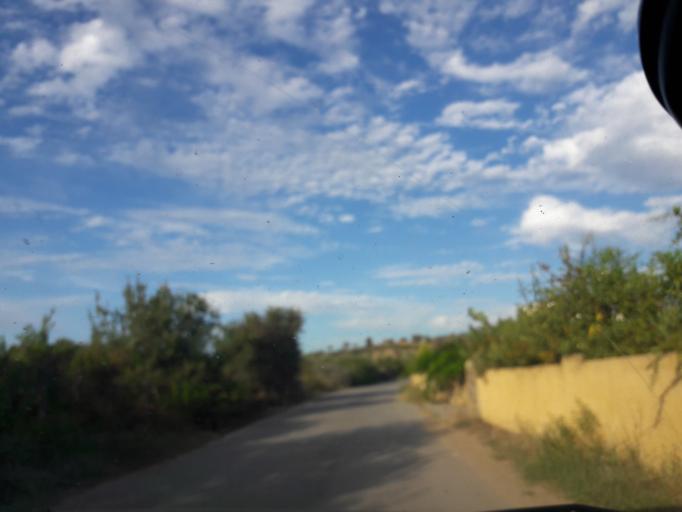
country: GR
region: Central Macedonia
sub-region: Nomos Chalkidikis
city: Nea Roda
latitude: 40.3341
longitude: 23.8993
